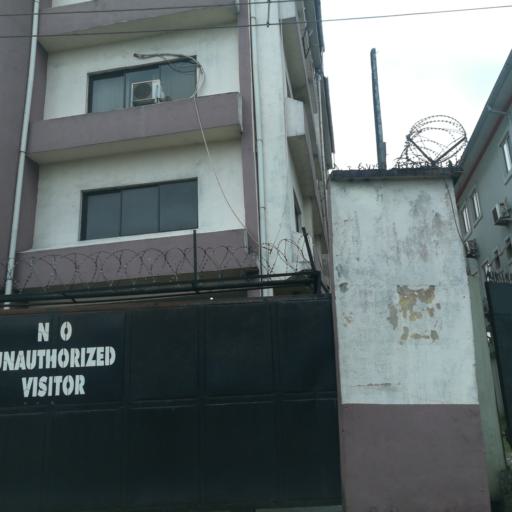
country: NG
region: Rivers
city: Port Harcourt
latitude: 4.8326
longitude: 7.0322
